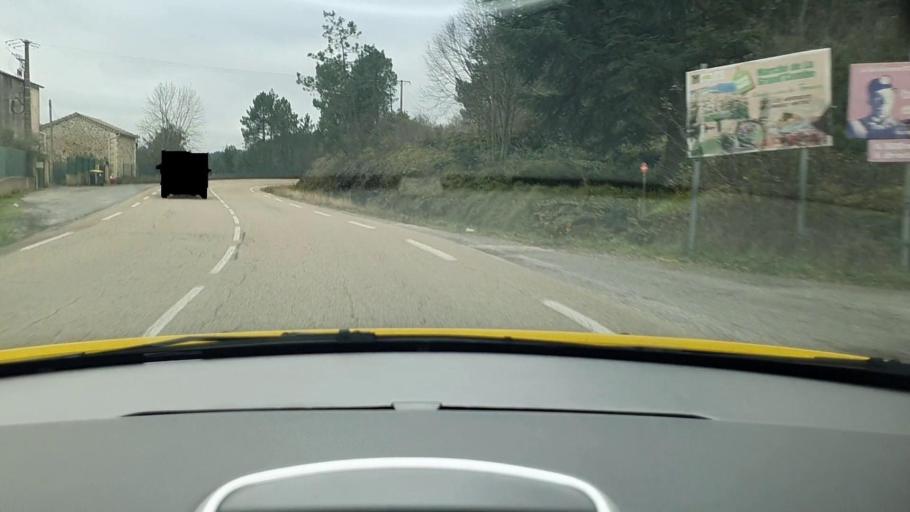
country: FR
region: Languedoc-Roussillon
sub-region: Departement du Gard
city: Laval-Pradel
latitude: 44.2386
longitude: 4.0556
